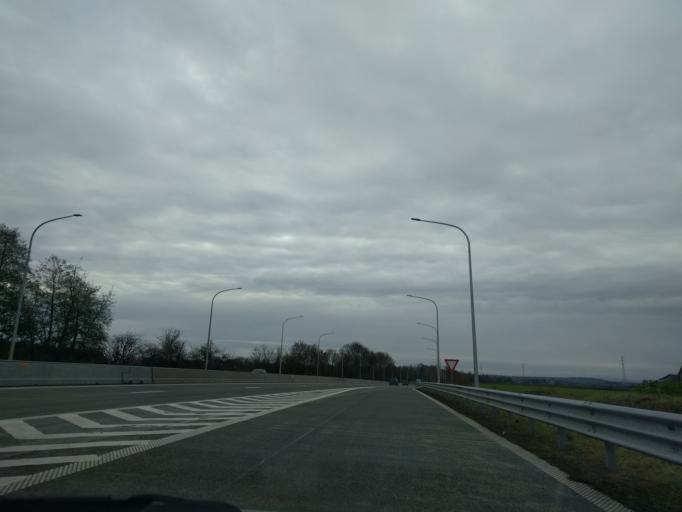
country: BE
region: Wallonia
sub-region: Province de Namur
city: Philippeville
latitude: 50.1921
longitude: 4.5301
